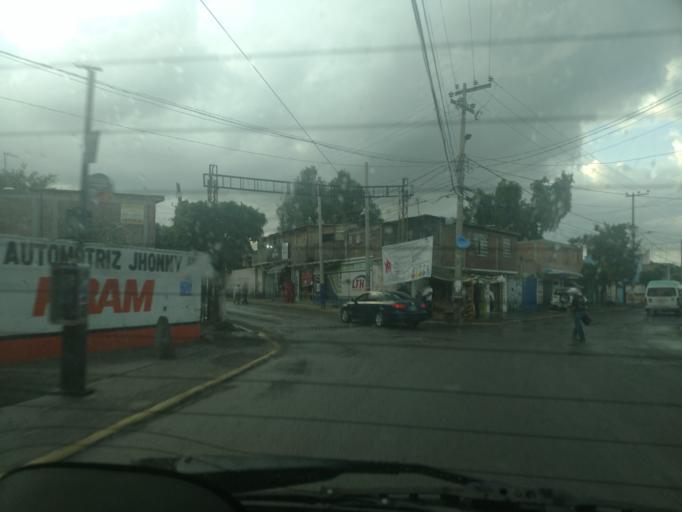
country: MX
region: Morelos
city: Coyotepec
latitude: 19.7713
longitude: -99.2015
